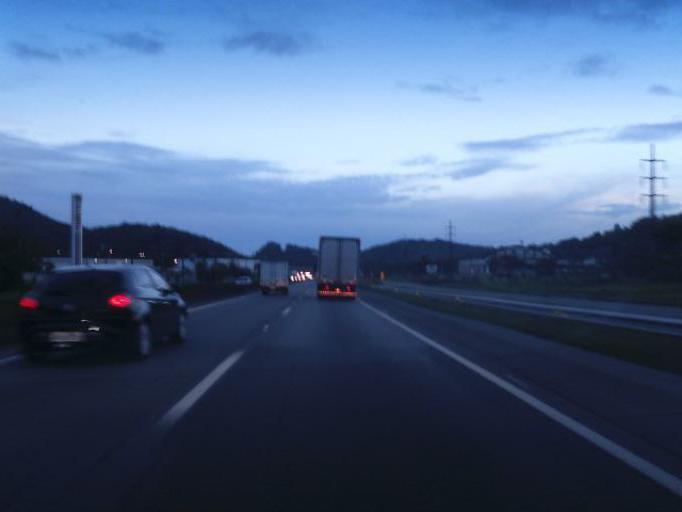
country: BR
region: Santa Catarina
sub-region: Joinville
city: Joinville
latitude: -26.3037
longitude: -48.8821
